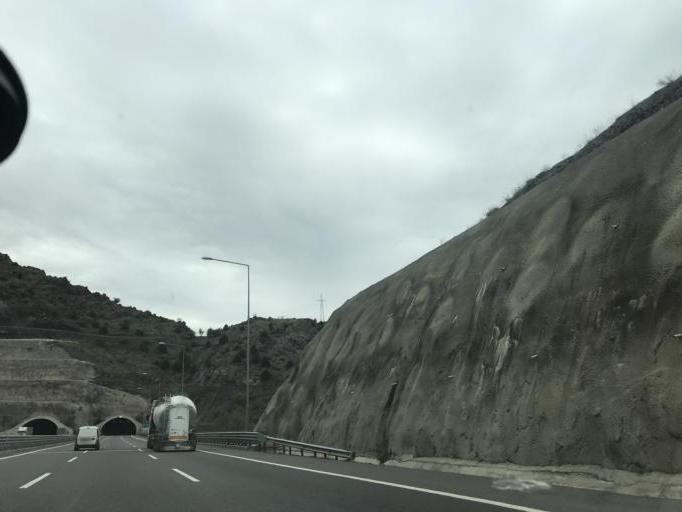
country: TR
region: Nigde
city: Ciftehan
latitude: 37.5565
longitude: 34.7675
